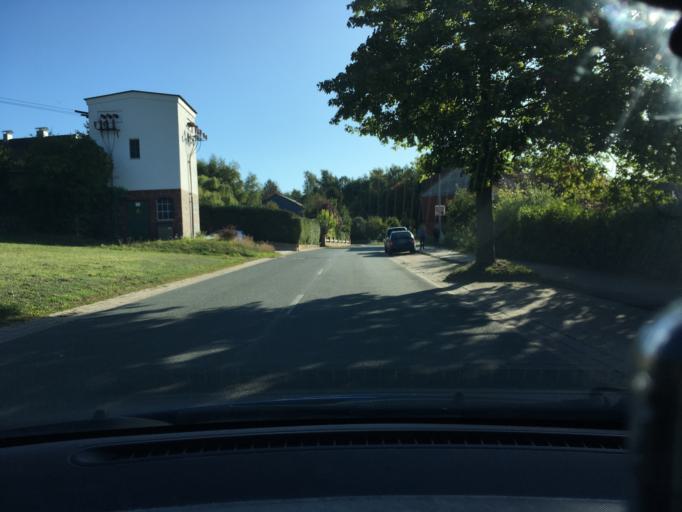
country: DE
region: Lower Saxony
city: Barsinghausen
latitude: 52.2586
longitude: 9.4502
